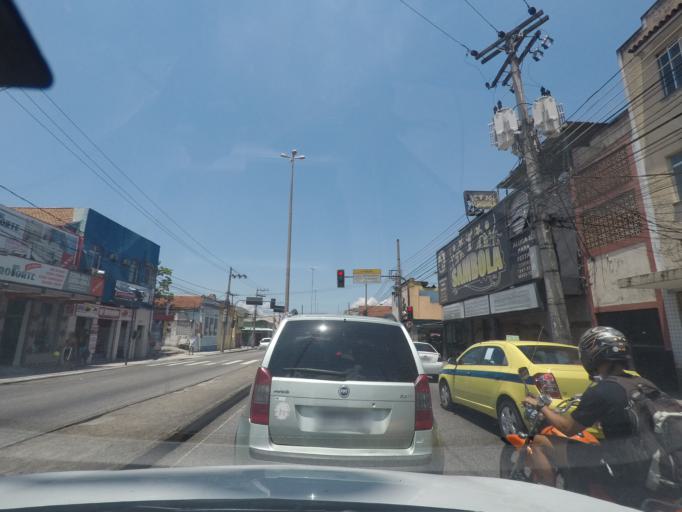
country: BR
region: Rio de Janeiro
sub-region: Rio De Janeiro
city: Rio de Janeiro
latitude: -22.8863
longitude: -43.3027
